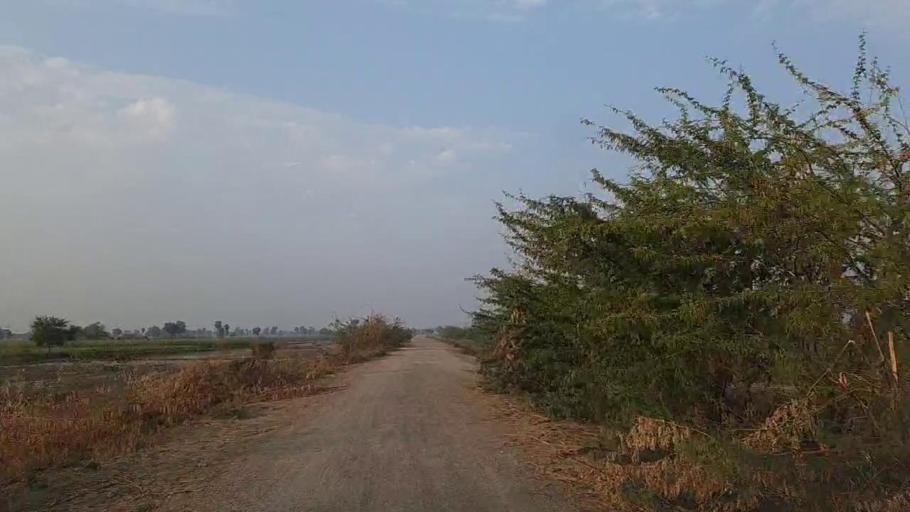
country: PK
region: Sindh
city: Jam Sahib
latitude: 26.3053
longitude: 68.6088
